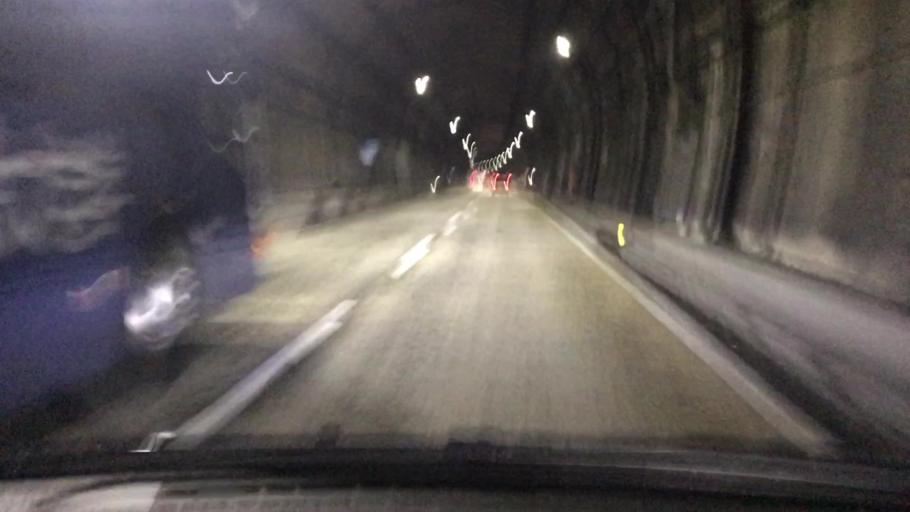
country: JP
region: Hyogo
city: Kobe
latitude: 34.7223
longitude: 135.1849
